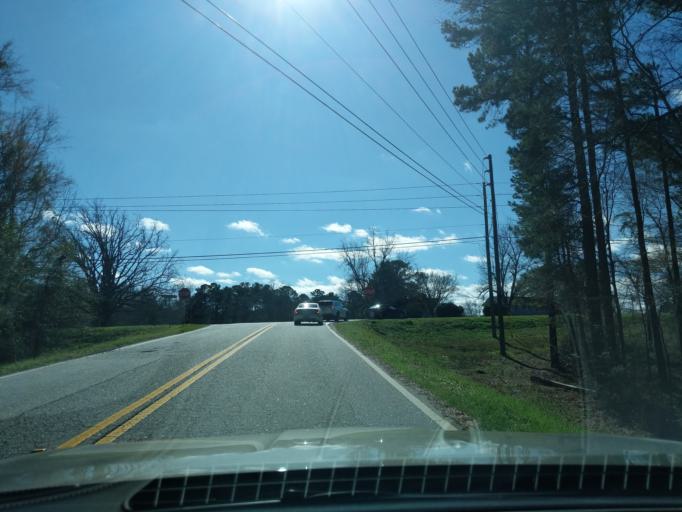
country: US
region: Georgia
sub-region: Columbia County
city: Evans
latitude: 33.5308
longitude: -82.1674
